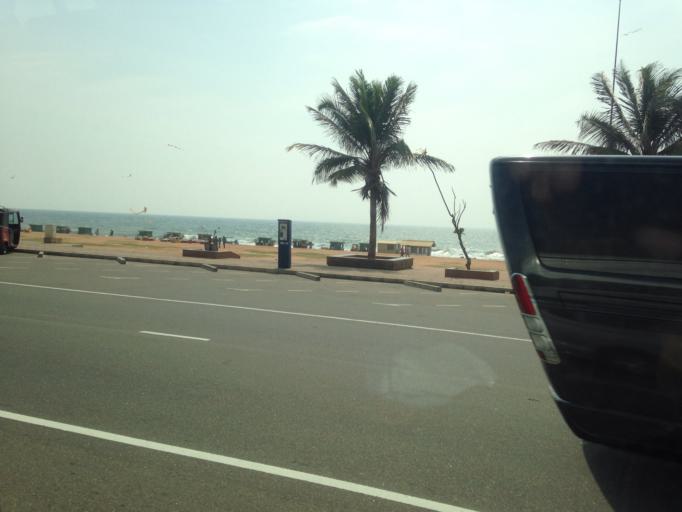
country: LK
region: Western
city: Colombo
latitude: 6.9249
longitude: 79.8450
